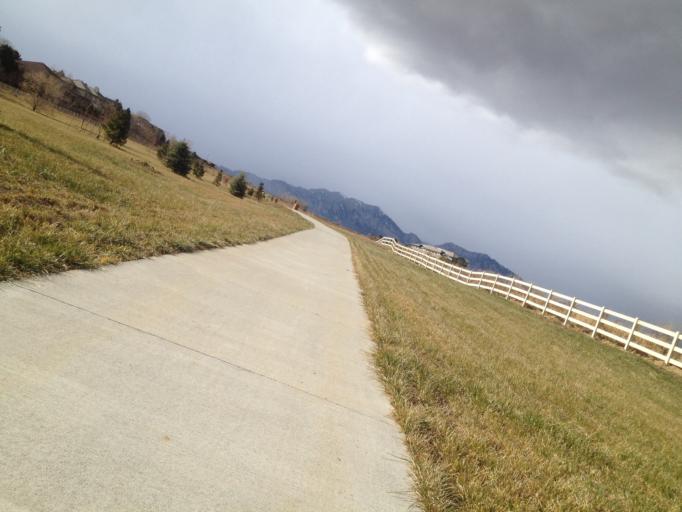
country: US
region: Colorado
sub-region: Boulder County
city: Superior
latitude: 39.9475
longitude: -105.1565
